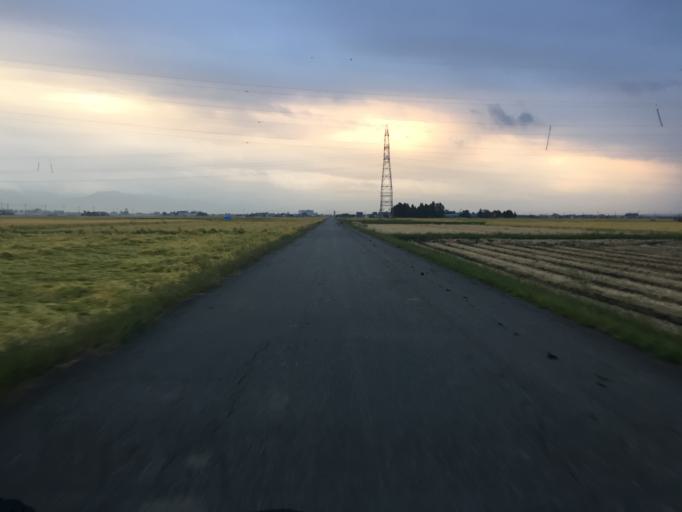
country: JP
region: Fukushima
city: Kitakata
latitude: 37.5771
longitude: 139.9072
